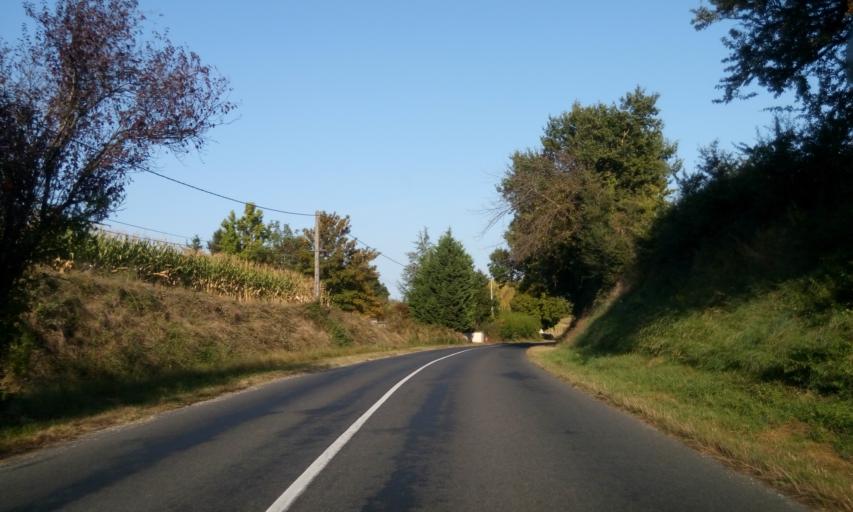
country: FR
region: Rhone-Alpes
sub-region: Departement de l'Ain
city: Ars-sur-Formans
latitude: 45.9973
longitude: 4.8300
